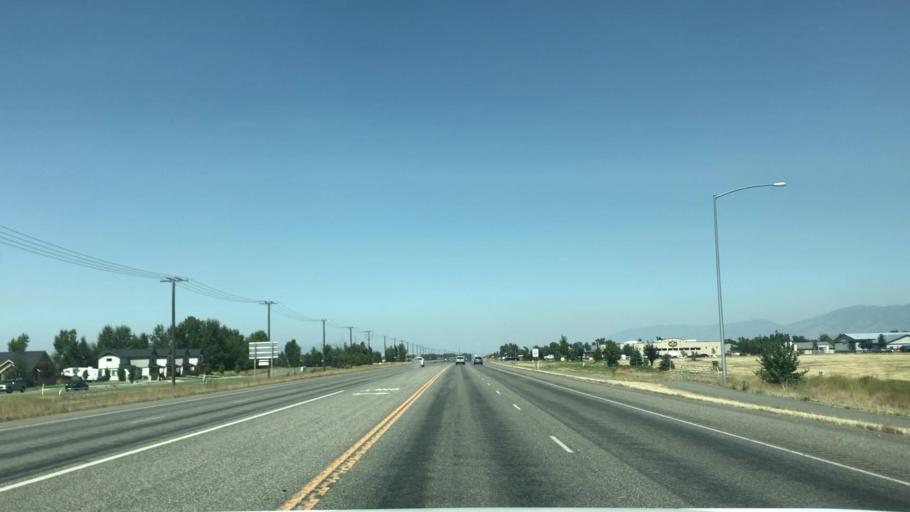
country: US
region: Montana
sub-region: Gallatin County
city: Four Corners
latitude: 45.6795
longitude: -111.1858
